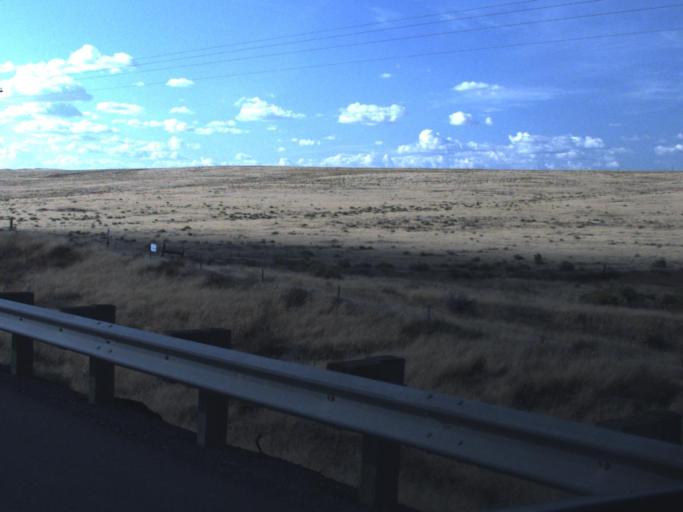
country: US
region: Oregon
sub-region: Morrow County
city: Irrigon
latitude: 45.9446
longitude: -119.5089
